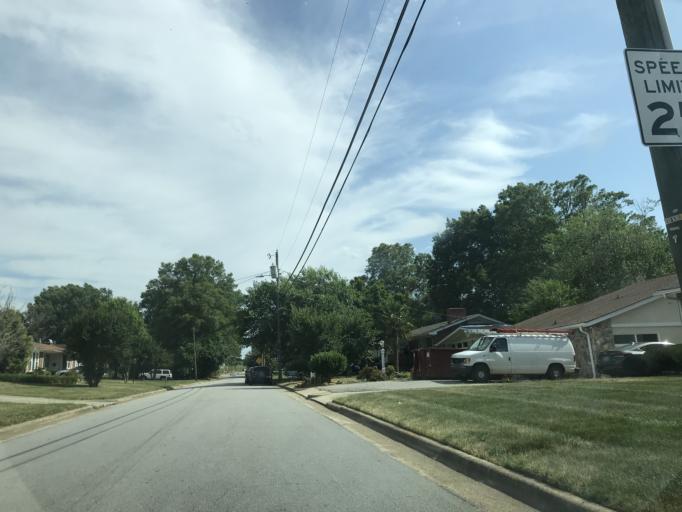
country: US
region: North Carolina
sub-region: Wake County
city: Raleigh
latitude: 35.7892
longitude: -78.6152
